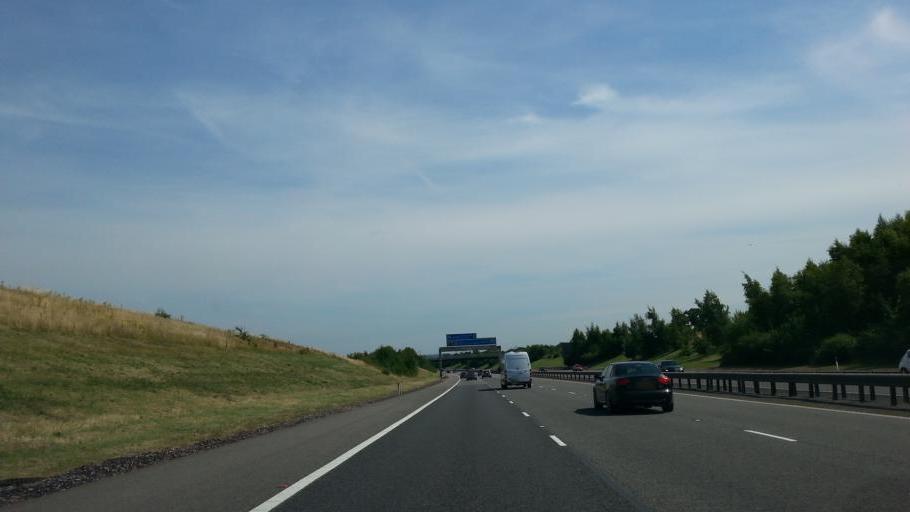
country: GB
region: England
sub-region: Warwickshire
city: Curdworth
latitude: 52.5588
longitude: -1.7502
